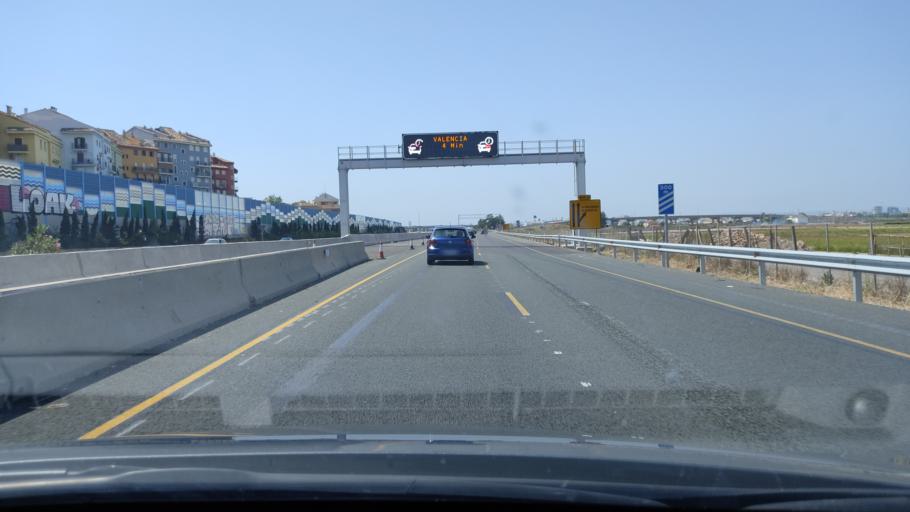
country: ES
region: Valencia
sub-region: Provincia de Valencia
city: Meliana
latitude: 39.5138
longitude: -0.3218
